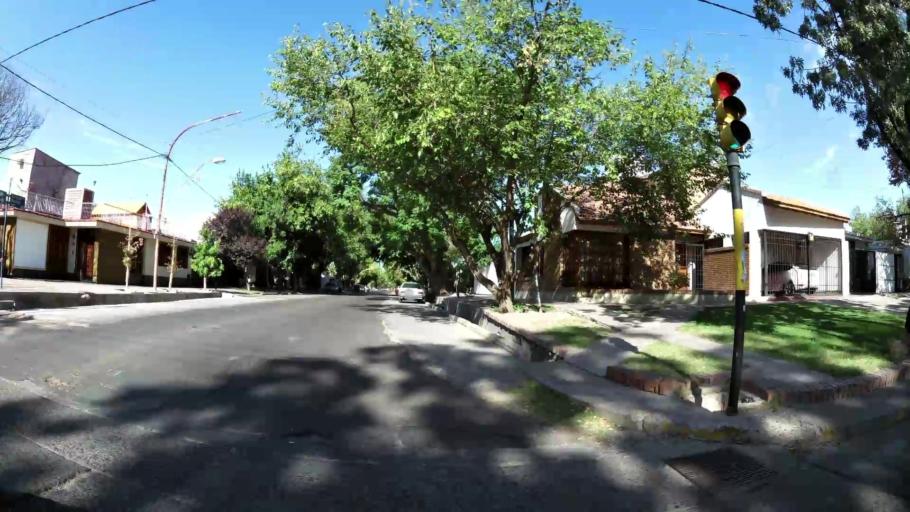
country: AR
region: Mendoza
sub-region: Departamento de Godoy Cruz
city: Godoy Cruz
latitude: -32.9131
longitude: -68.8334
